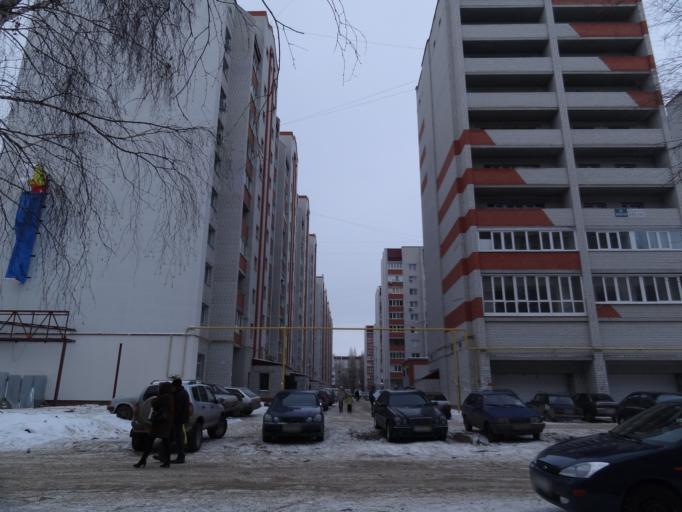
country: RU
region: Saratov
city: Engel's
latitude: 51.4774
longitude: 46.1355
